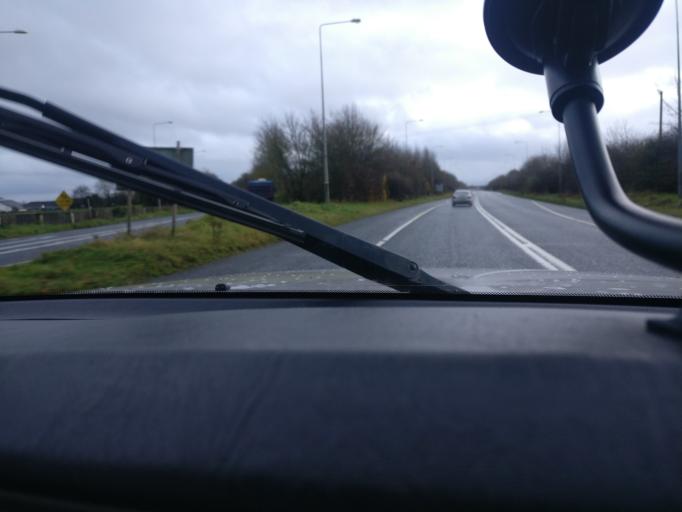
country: IE
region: Leinster
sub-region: Kildare
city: Kilcock
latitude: 53.4095
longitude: -6.7033
